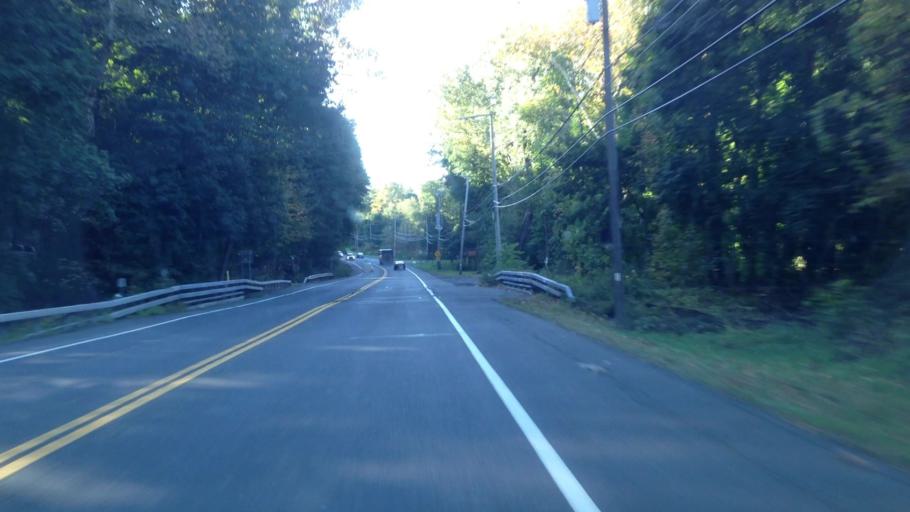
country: US
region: New York
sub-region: Dutchess County
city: Hyde Park
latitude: 41.8188
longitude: -73.9642
